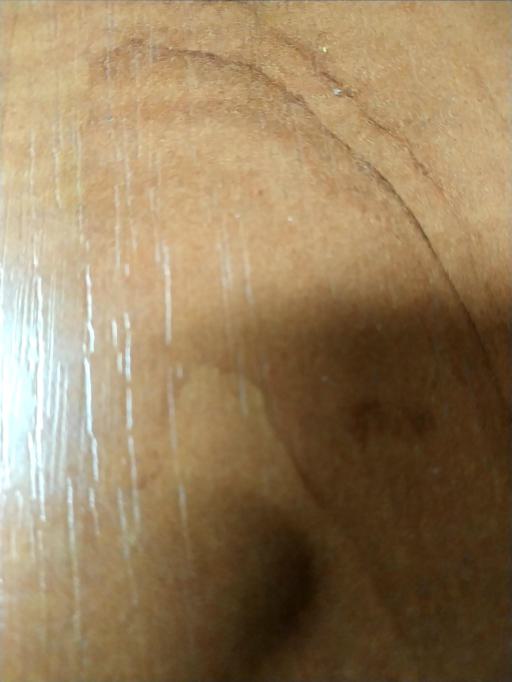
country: RU
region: Smolensk
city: Yartsevo
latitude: 55.4323
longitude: 32.8230
